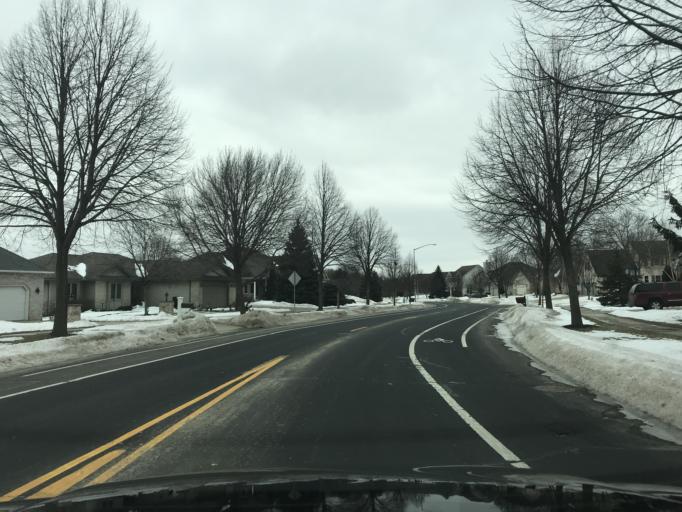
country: US
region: Wisconsin
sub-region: Dane County
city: Monona
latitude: 43.0823
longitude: -89.2730
